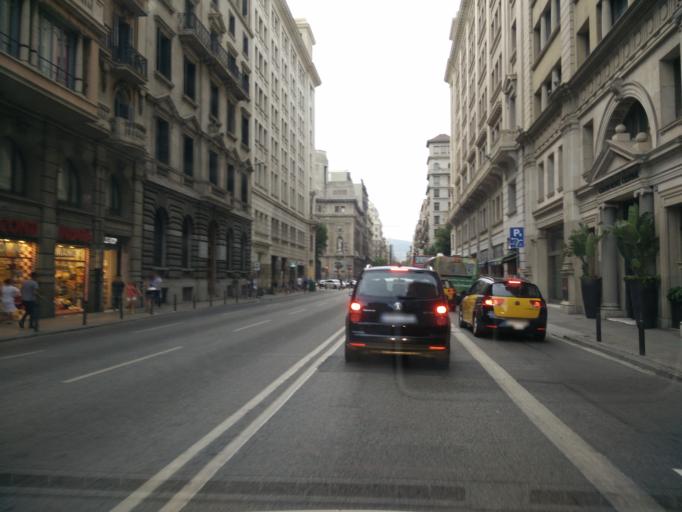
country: ES
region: Catalonia
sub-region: Provincia de Barcelona
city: Ciutat Vella
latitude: 41.3848
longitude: 2.1777
